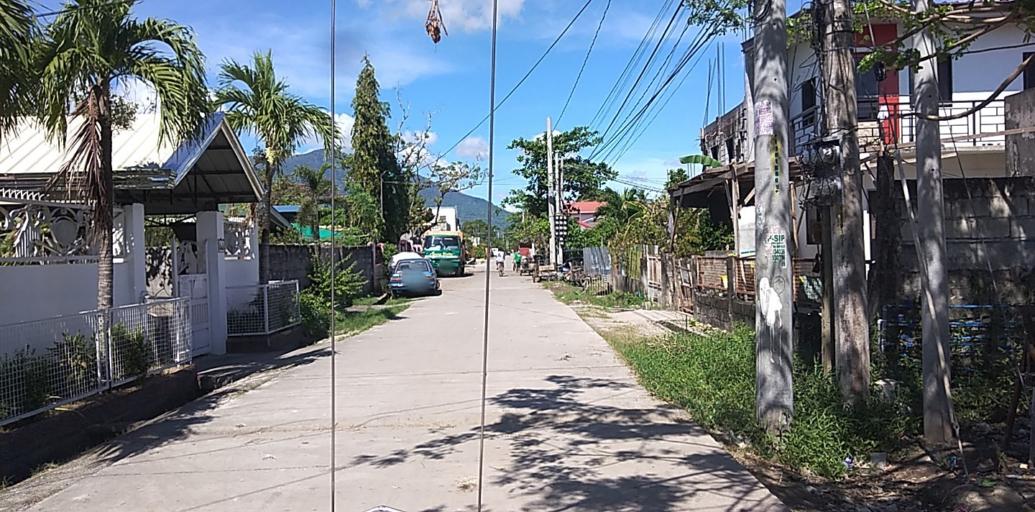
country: PH
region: Central Luzon
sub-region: Province of Pampanga
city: Arayat
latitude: 15.1344
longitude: 120.7754
